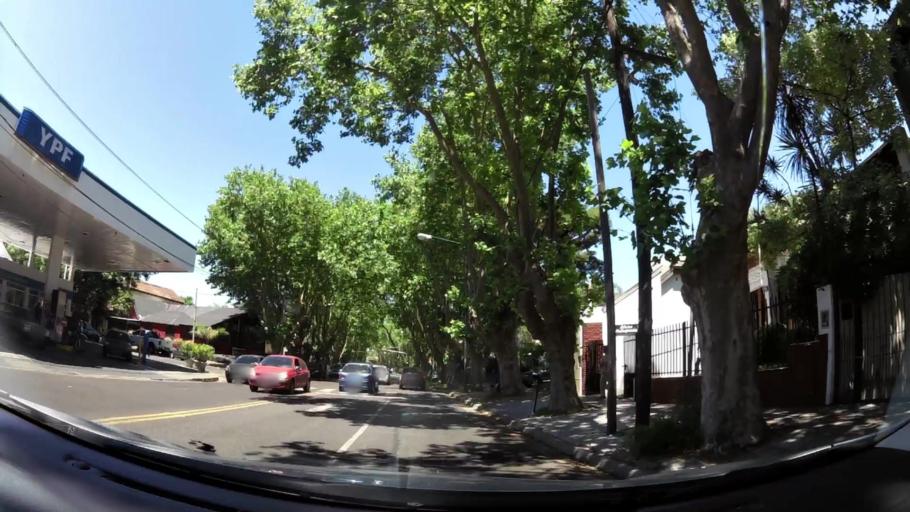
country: AR
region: Buenos Aires
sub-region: Partido de San Isidro
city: San Isidro
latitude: -34.4539
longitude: -58.5259
